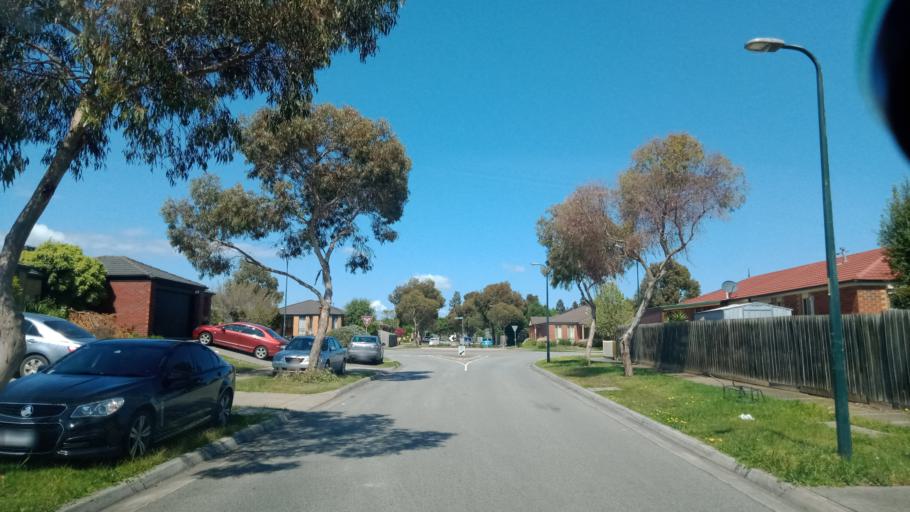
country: AU
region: Victoria
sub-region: Casey
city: Cranbourne West
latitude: -38.0944
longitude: 145.2584
